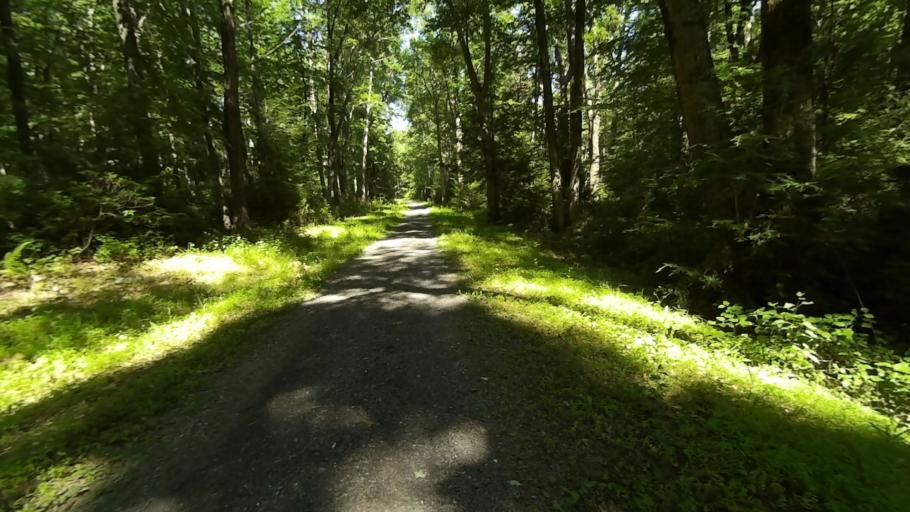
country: US
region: Pennsylvania
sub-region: Centre County
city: Boalsburg
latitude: 40.7384
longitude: -77.7579
